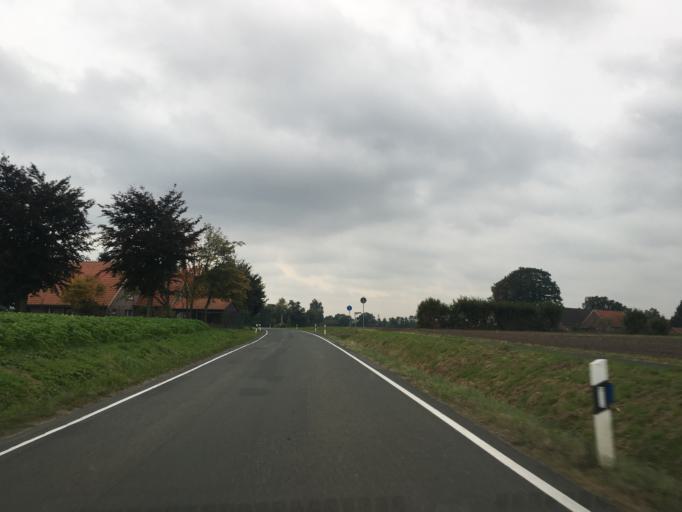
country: DE
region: North Rhine-Westphalia
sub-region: Regierungsbezirk Munster
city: Nordwalde
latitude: 52.1117
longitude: 7.4592
